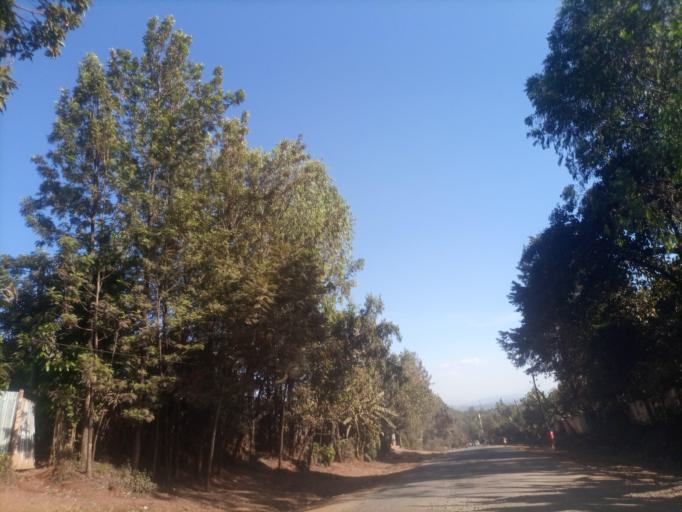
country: ET
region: Oromiya
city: Jima
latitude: 7.6978
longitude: 36.8154
